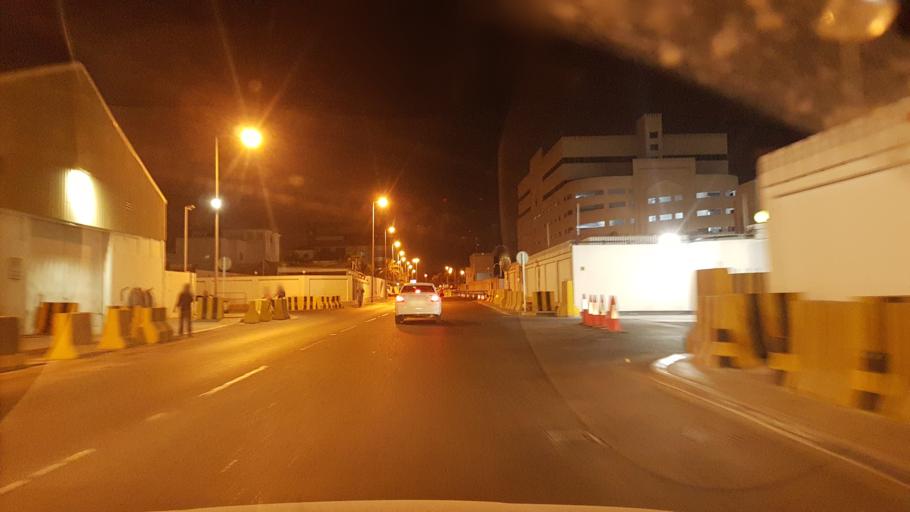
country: BH
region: Manama
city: Manama
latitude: 26.2229
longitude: 50.5778
